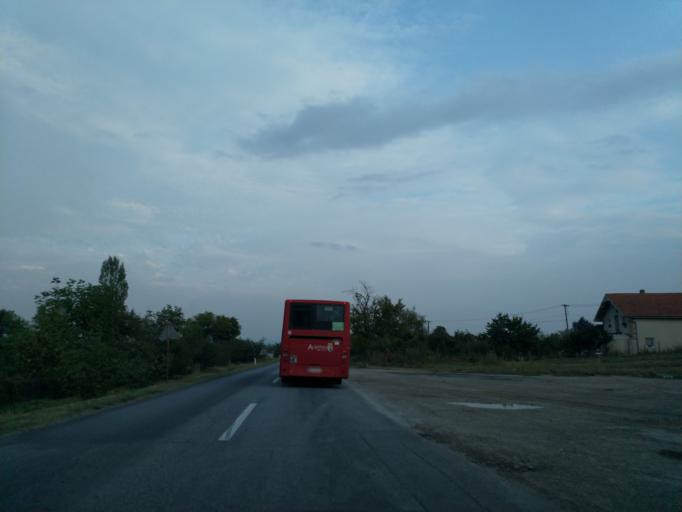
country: RS
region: Central Serbia
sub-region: Sumadijski Okrug
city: Kragujevac
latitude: 44.1333
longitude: 20.8108
